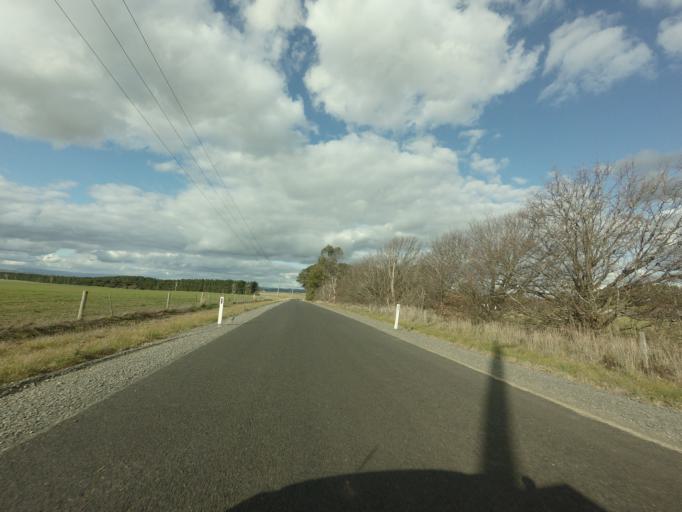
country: AU
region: Tasmania
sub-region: Northern Midlands
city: Longford
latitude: -41.8066
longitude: 147.1770
